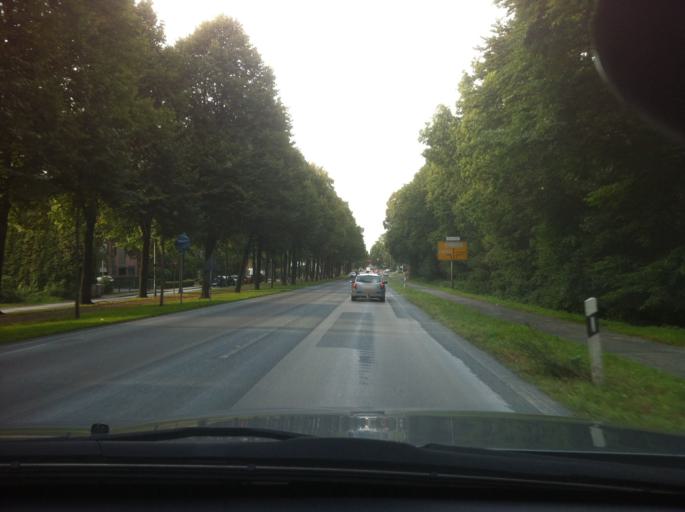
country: DE
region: North Rhine-Westphalia
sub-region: Regierungsbezirk Dusseldorf
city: Kleve
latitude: 51.7711
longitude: 6.1399
